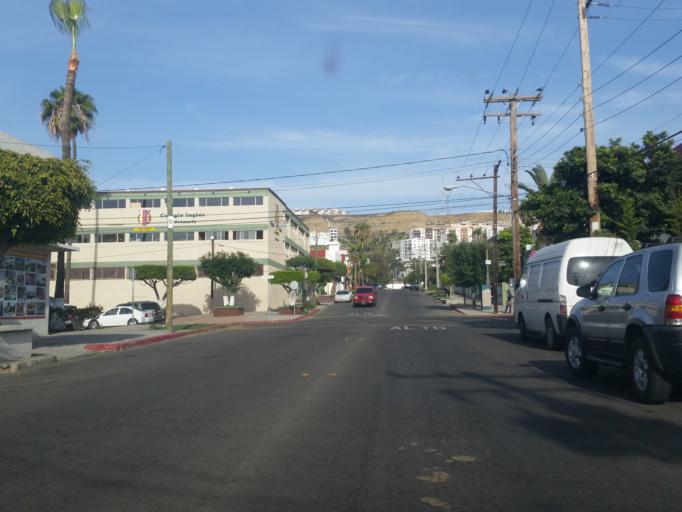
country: US
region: California
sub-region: San Diego County
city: Imperial Beach
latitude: 32.5250
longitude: -117.1128
